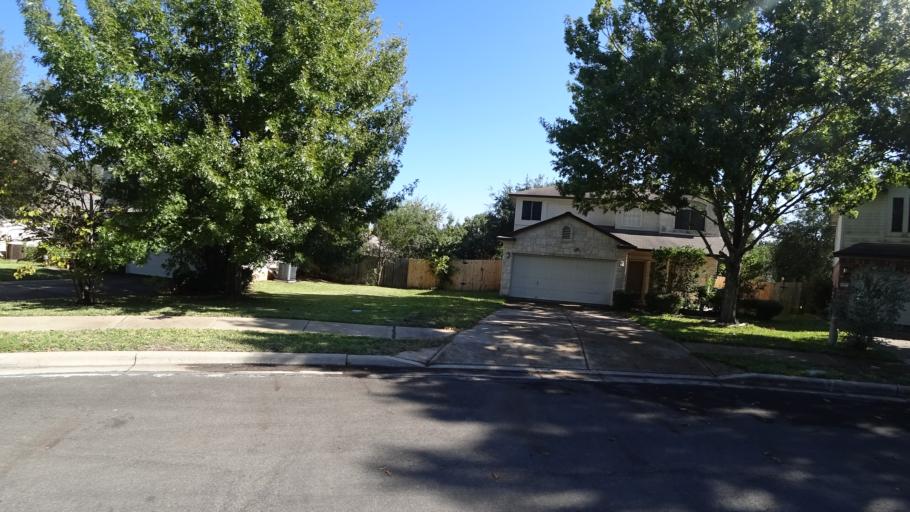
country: US
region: Texas
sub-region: Travis County
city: Shady Hollow
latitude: 30.2011
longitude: -97.8596
